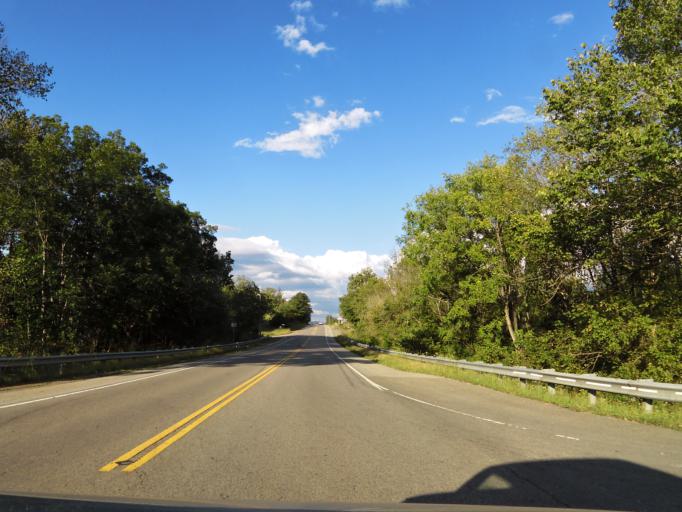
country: US
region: Tennessee
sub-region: Grainger County
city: Rutledge
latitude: 36.2431
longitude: -83.6060
